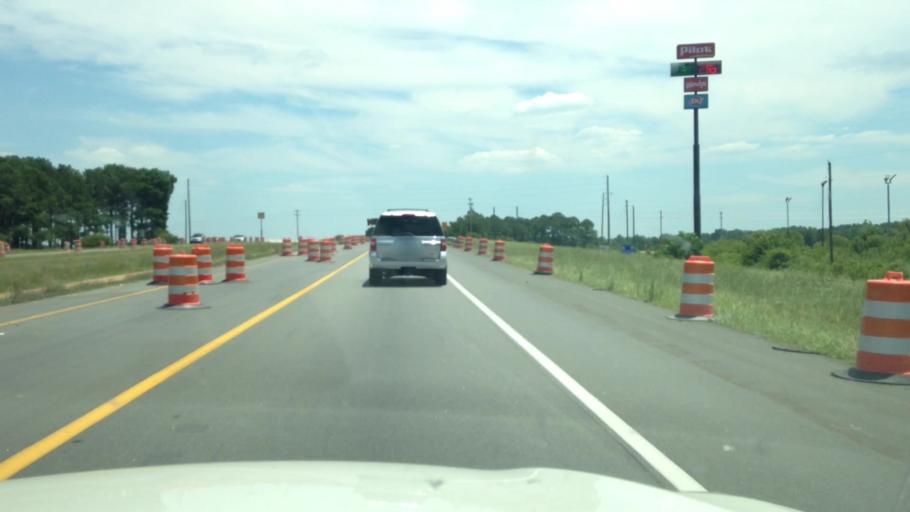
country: US
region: South Carolina
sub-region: Lee County
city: Bishopville
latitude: 34.1948
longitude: -80.2837
